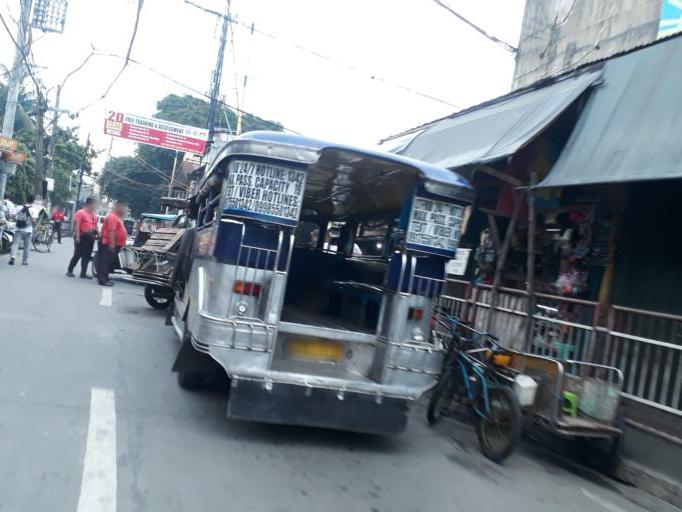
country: PH
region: Calabarzon
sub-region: Province of Rizal
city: Malabon
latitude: 14.6721
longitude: 120.9366
